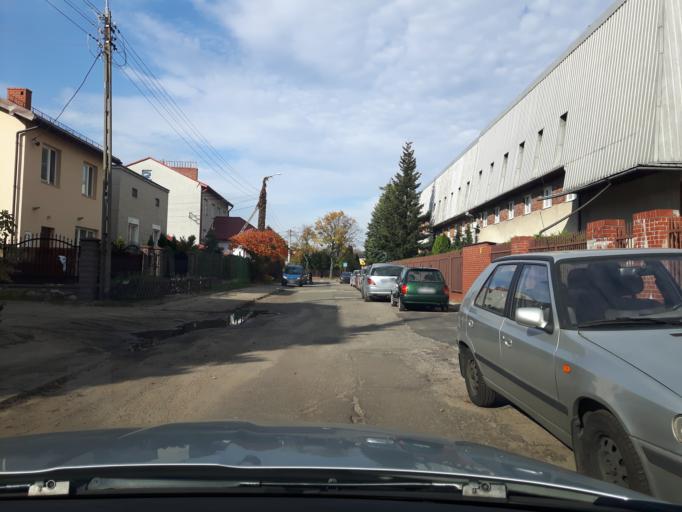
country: PL
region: Masovian Voivodeship
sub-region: Powiat wolominski
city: Zabki
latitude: 52.2989
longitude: 21.0973
